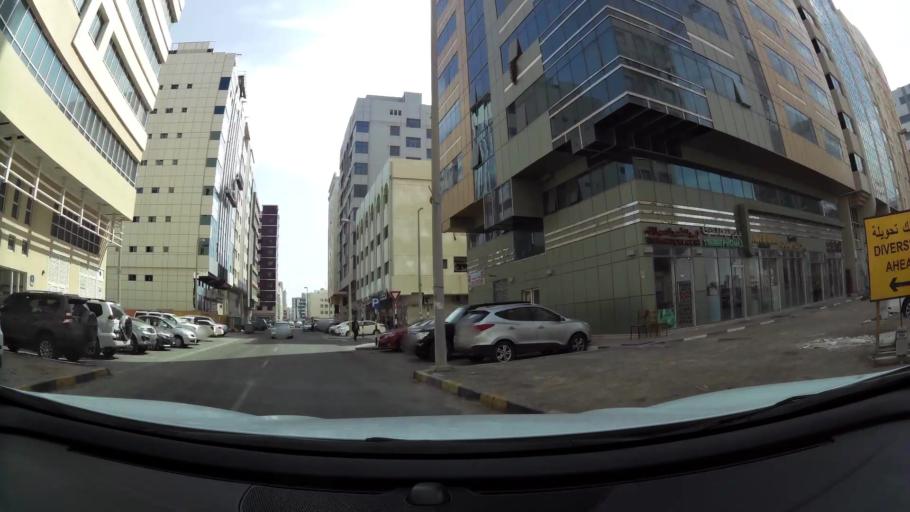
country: AE
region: Abu Dhabi
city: Abu Dhabi
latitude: 24.3374
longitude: 54.5342
